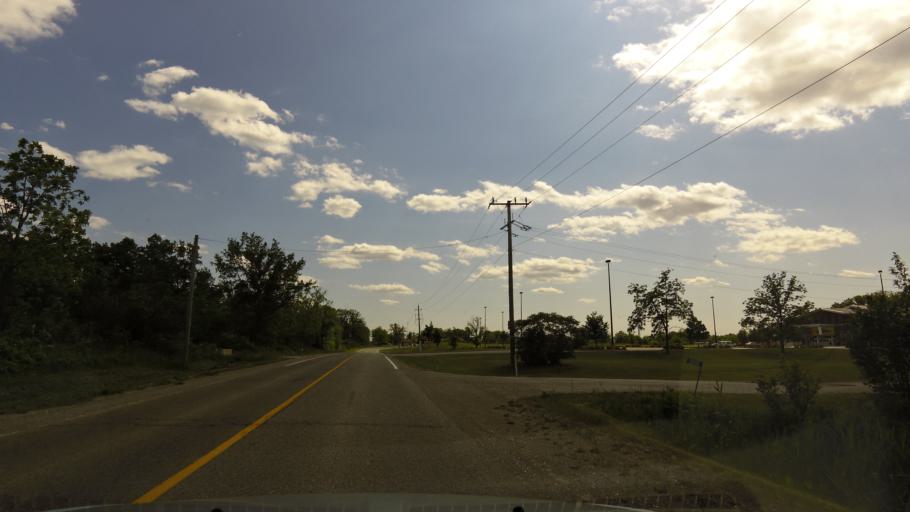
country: CA
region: Ontario
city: Ancaster
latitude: 43.1051
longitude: -80.0919
